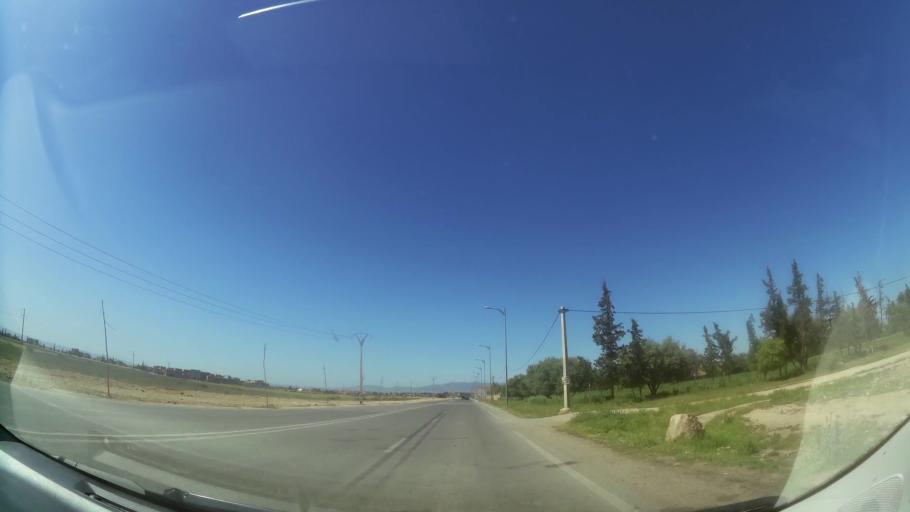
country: MA
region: Oriental
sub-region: Oujda-Angad
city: Oujda
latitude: 34.6920
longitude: -1.8571
